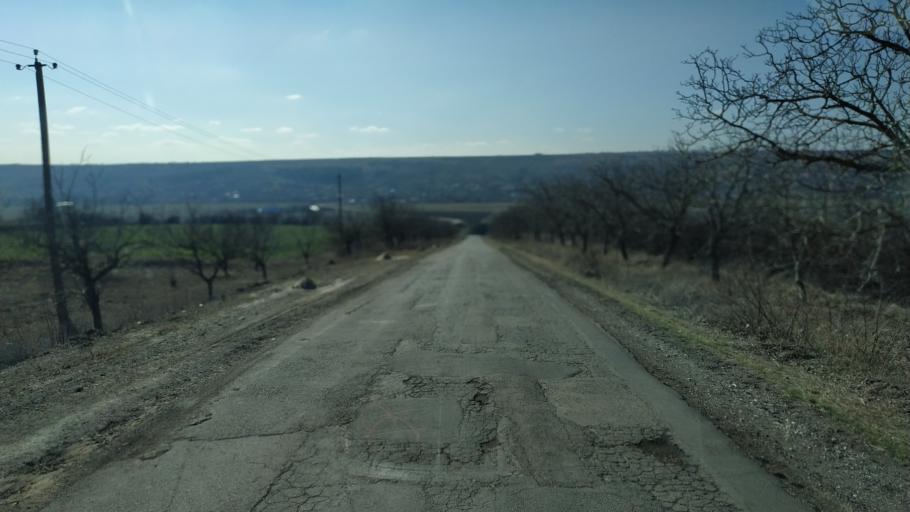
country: MD
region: Hincesti
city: Hincesti
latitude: 46.7583
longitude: 28.6609
